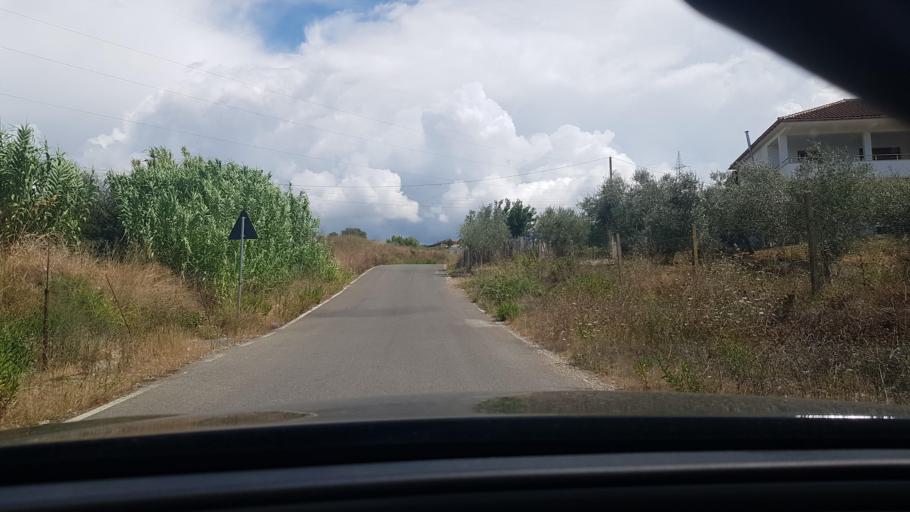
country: AL
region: Durres
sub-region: Rrethi i Durresit
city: Rrashbull
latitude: 41.2975
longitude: 19.5250
